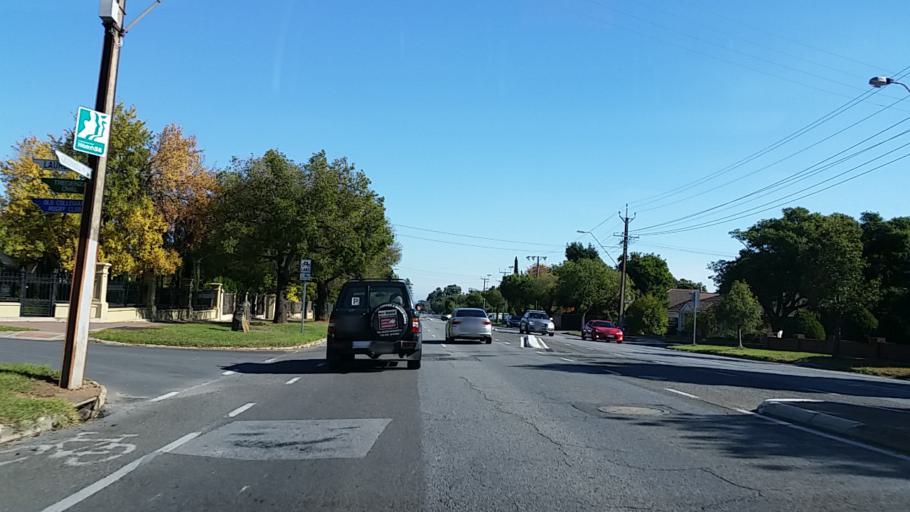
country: AU
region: South Australia
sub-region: Burnside
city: Tusmore
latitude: -34.9389
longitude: 138.6496
